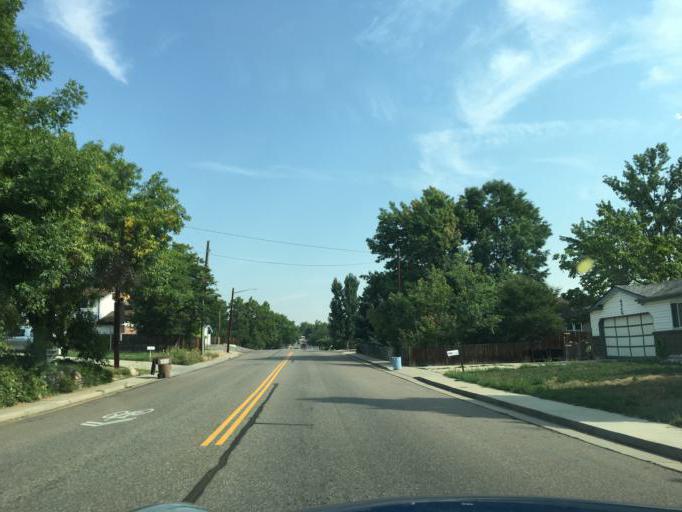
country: US
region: Colorado
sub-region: Jefferson County
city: Arvada
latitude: 39.8226
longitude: -105.0674
